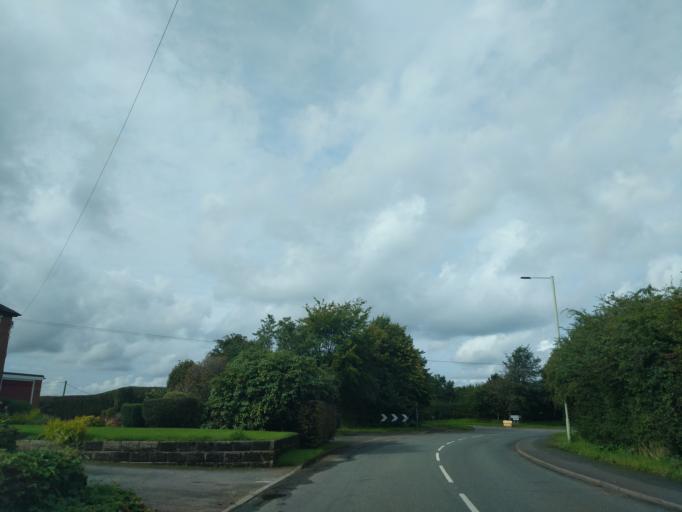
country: GB
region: England
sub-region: Staffordshire
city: Audley
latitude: 53.0084
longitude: -2.2969
